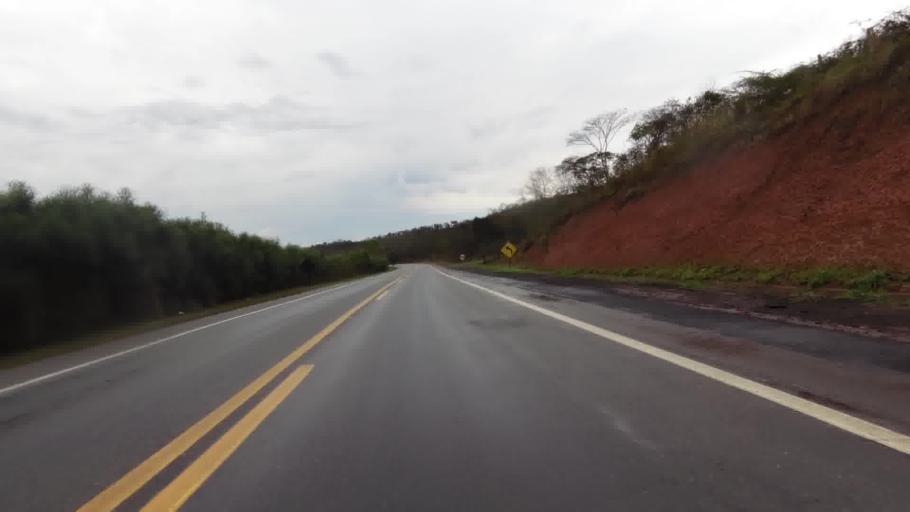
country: BR
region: Rio de Janeiro
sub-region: Campos Dos Goytacazes
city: Campos
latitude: -21.4897
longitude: -41.3413
